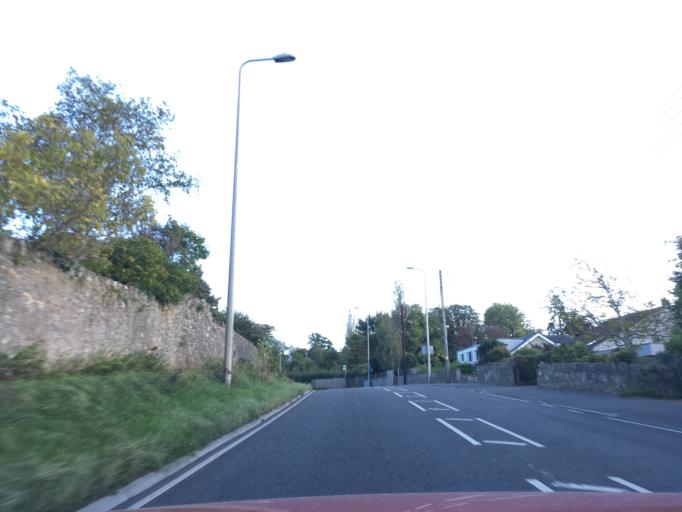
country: GB
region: England
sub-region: North Somerset
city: Long Ashton
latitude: 51.4627
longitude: -2.6666
